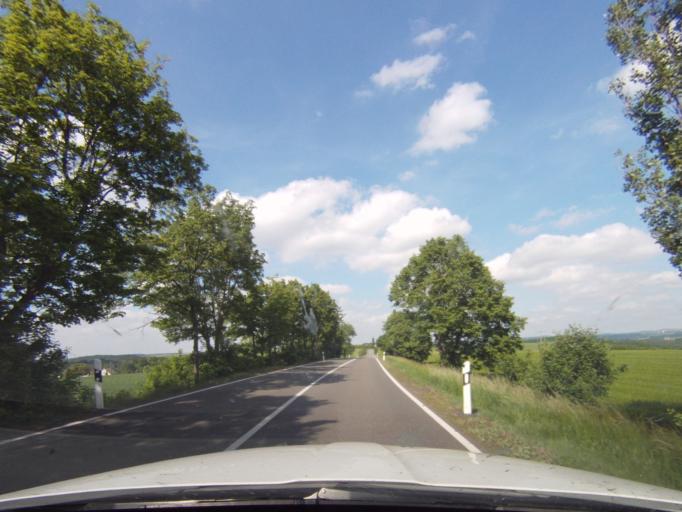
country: DE
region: Thuringia
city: Zedlitz
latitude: 50.8309
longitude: 12.0176
